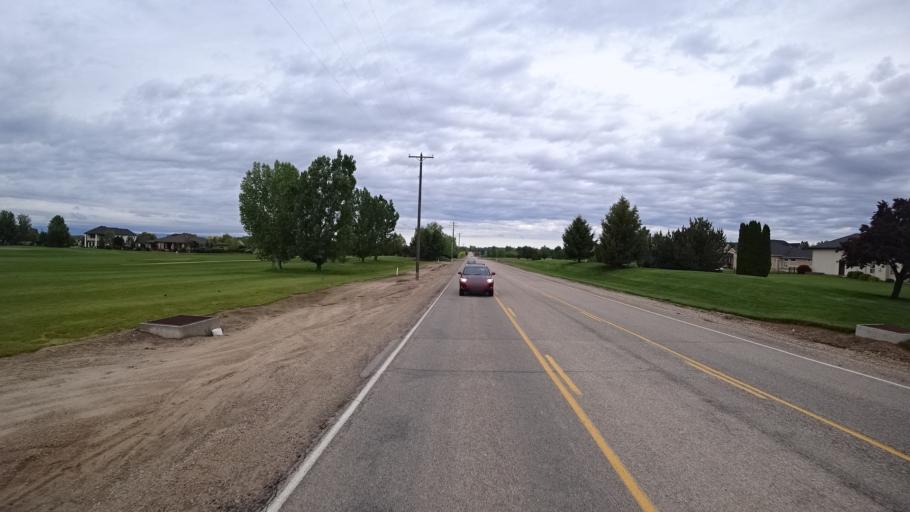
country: US
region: Idaho
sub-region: Ada County
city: Star
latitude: 43.7211
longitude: -116.4623
